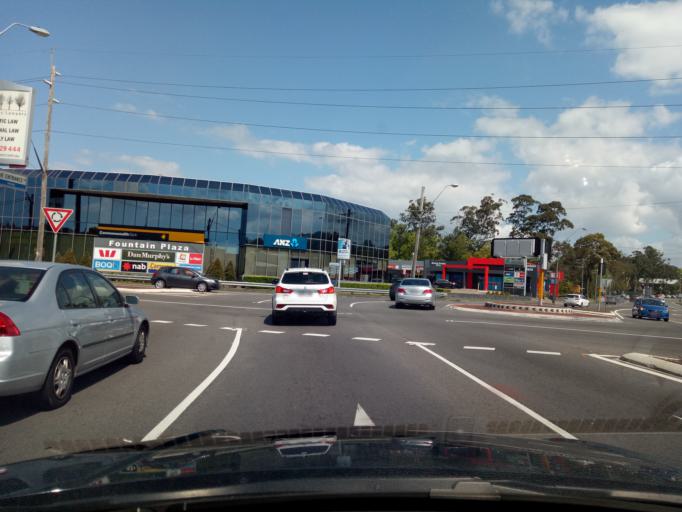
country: AU
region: New South Wales
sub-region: Gosford Shire
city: Erina
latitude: -33.4377
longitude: 151.3838
